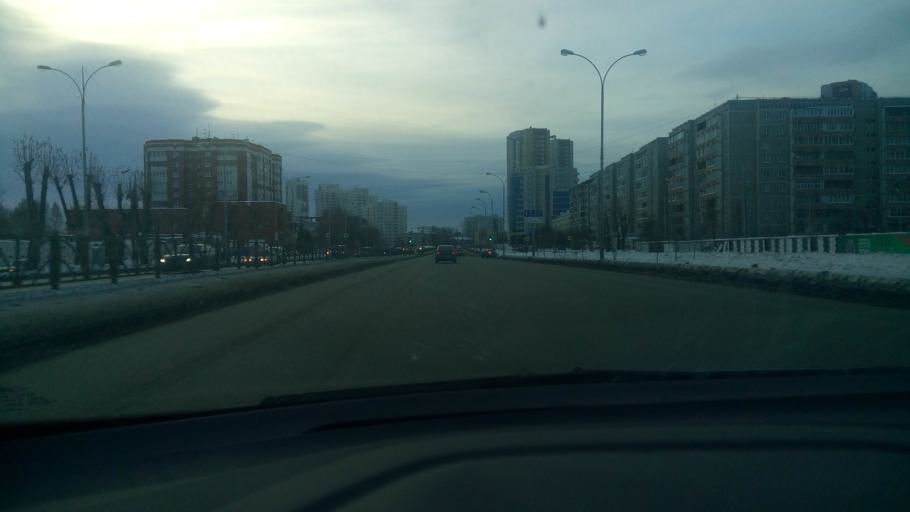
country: RU
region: Sverdlovsk
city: Yekaterinburg
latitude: 56.8090
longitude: 60.6303
